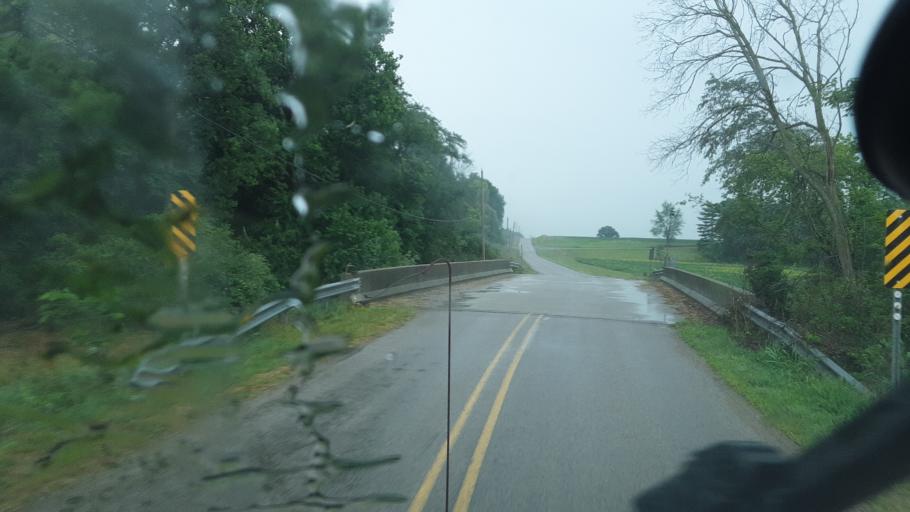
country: US
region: Indiana
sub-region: DeKalb County
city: Butler
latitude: 41.4656
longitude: -84.8141
